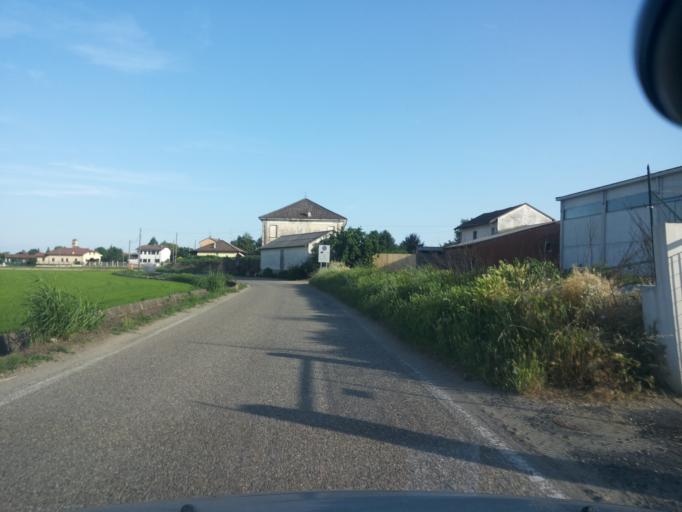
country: IT
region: Piedmont
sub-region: Provincia di Vercelli
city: Pezzana
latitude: 45.2656
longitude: 8.4764
